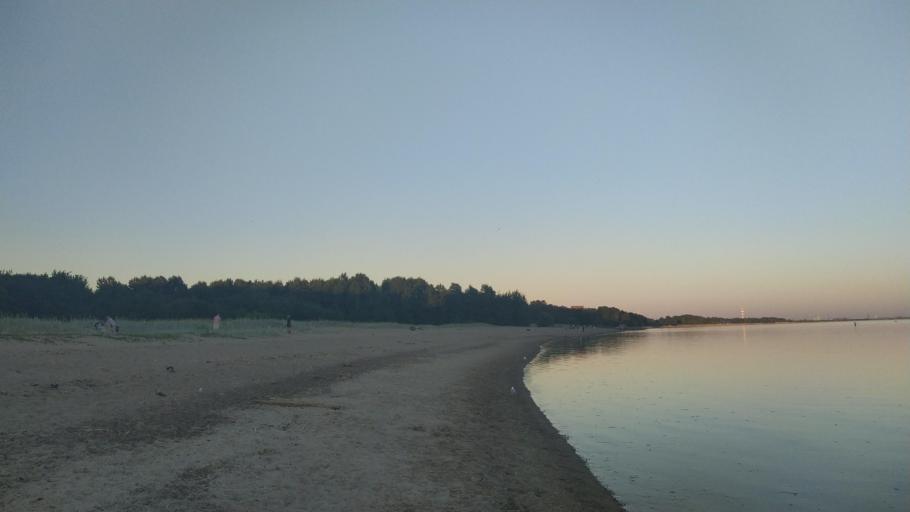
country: RU
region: St.-Petersburg
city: Kronshtadt
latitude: 60.0255
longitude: 29.6682
